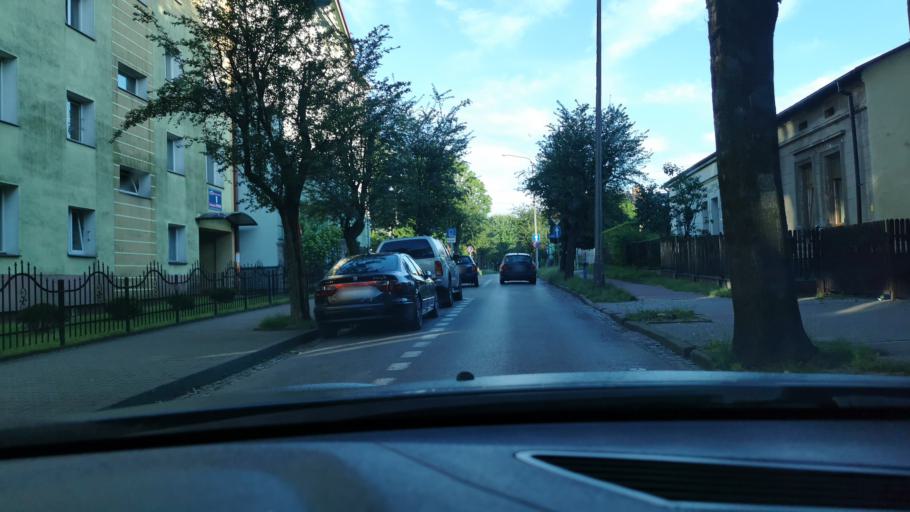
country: PL
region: Lesser Poland Voivodeship
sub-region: Powiat chrzanowski
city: Chrzanow
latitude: 50.1381
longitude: 19.3999
